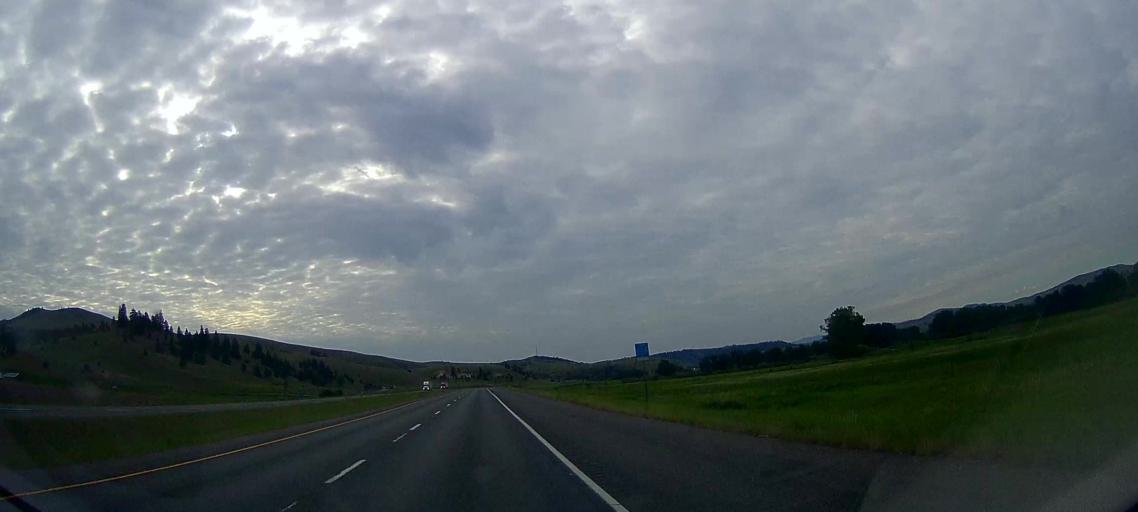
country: US
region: Montana
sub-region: Powell County
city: Deer Lodge
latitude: 46.6002
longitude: -112.9550
